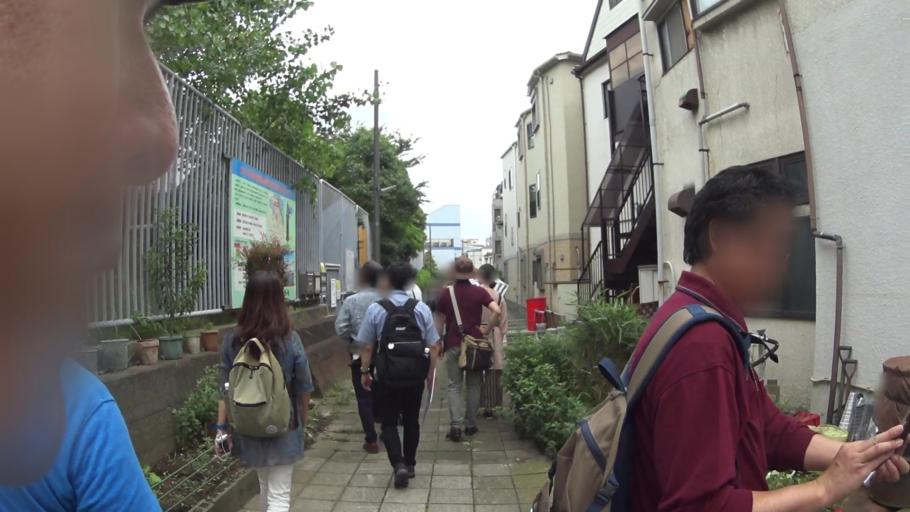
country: JP
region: Tokyo
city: Urayasu
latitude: 35.7166
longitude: 139.8388
